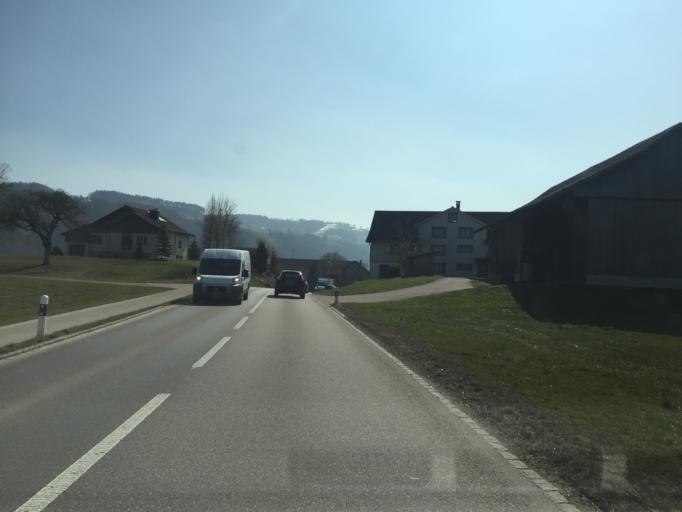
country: CH
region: Saint Gallen
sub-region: Wahlkreis Toggenburg
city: Lutisburg
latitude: 47.3817
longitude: 9.0727
